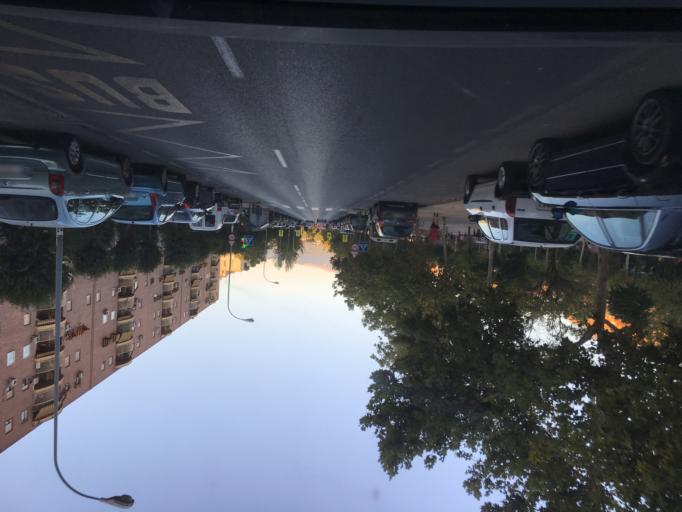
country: ES
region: Andalusia
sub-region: Provincia de Granada
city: Granada
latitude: 37.2023
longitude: -3.6101
